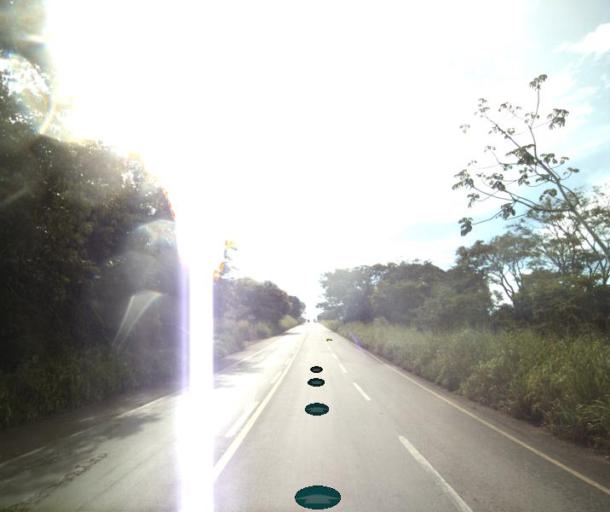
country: BR
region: Goias
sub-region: Jaragua
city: Jaragua
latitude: -15.6303
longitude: -49.3811
